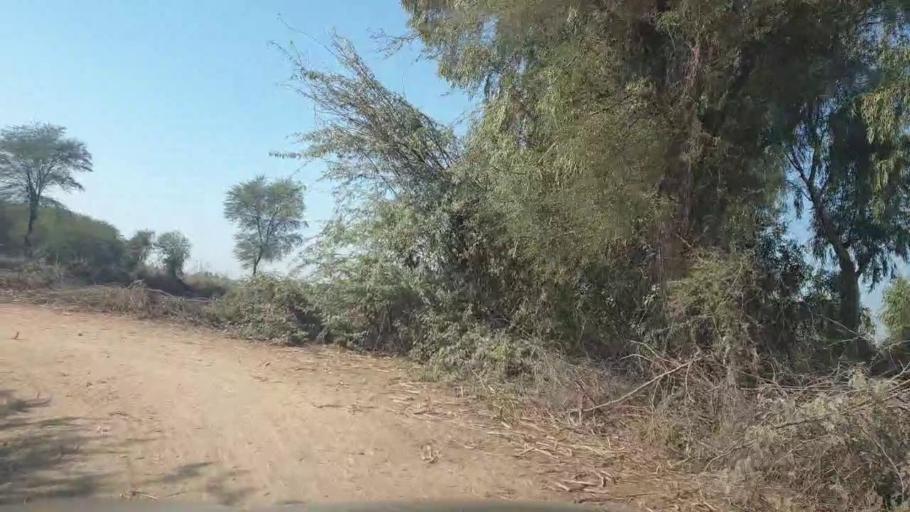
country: PK
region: Sindh
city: Mirpur Mathelo
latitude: 28.0983
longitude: 69.5279
